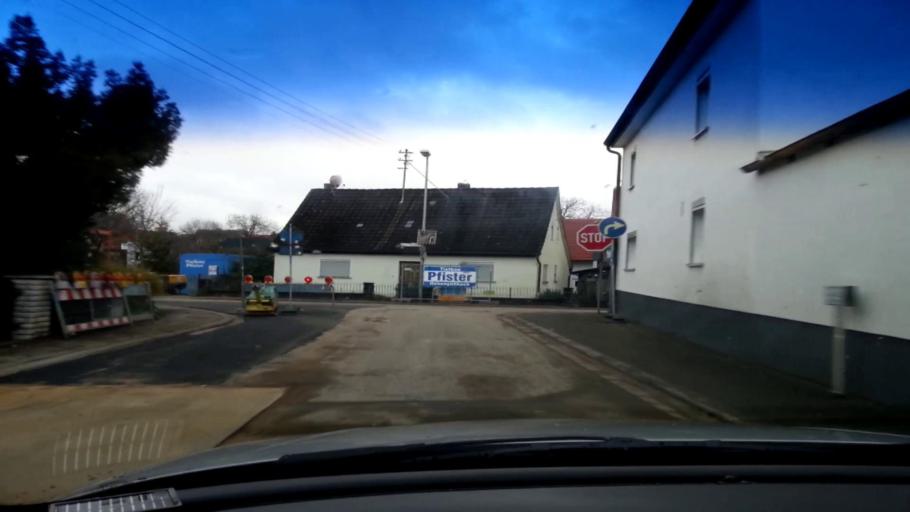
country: DE
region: Bavaria
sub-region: Upper Franconia
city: Litzendorf
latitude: 49.9255
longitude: 11.0041
